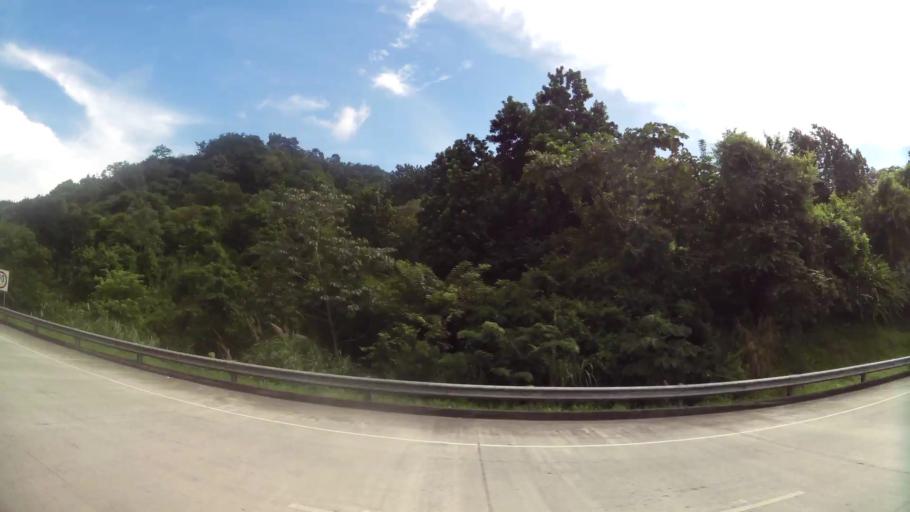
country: PA
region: Panama
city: San Miguelito
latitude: 9.0825
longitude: -79.4650
